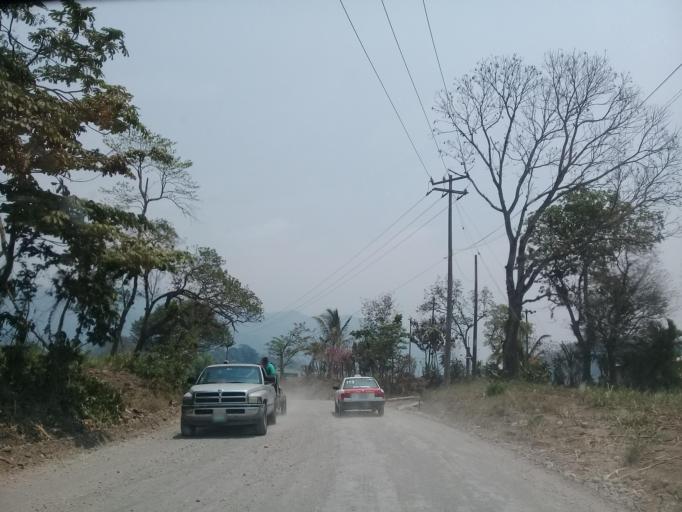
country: MX
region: Veracruz
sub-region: Tezonapa
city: Laguna Chica (Pueblo Nuevo)
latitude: 18.5664
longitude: -96.7206
